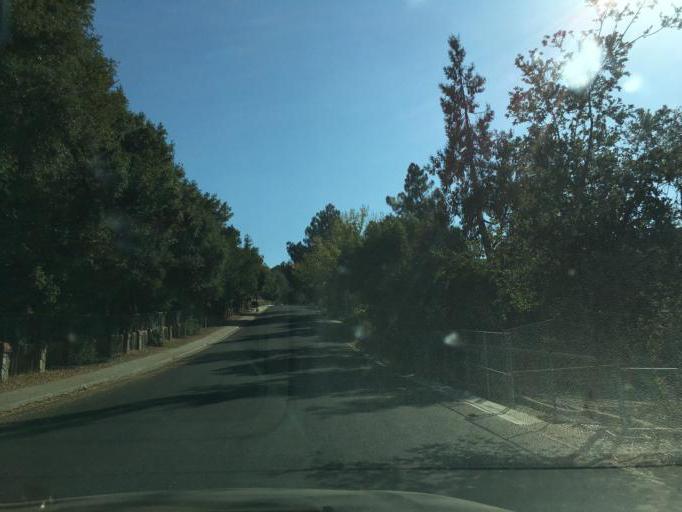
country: US
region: California
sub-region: Santa Clara County
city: Cambrian Park
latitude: 37.2300
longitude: -121.9129
